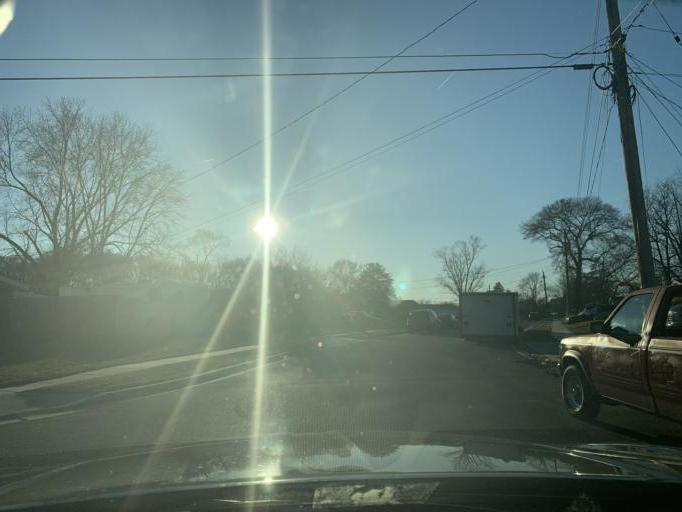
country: US
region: Maryland
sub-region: Anne Arundel County
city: South Gate
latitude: 39.1450
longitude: -76.6230
